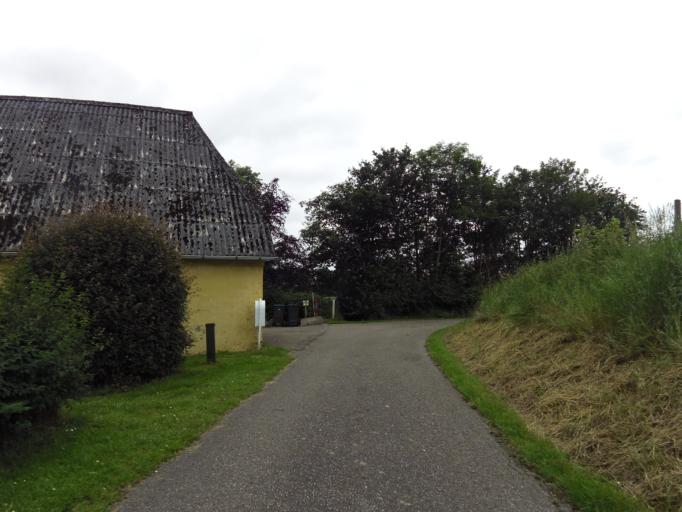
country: DK
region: South Denmark
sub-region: Tonder Kommune
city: Toftlund
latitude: 55.1021
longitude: 9.0842
